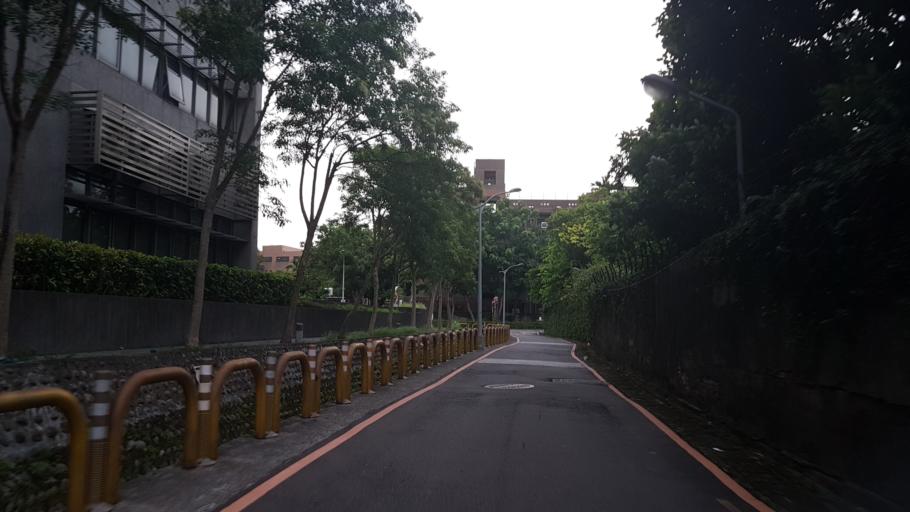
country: TW
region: Taipei
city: Taipei
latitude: 25.0138
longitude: 121.5475
